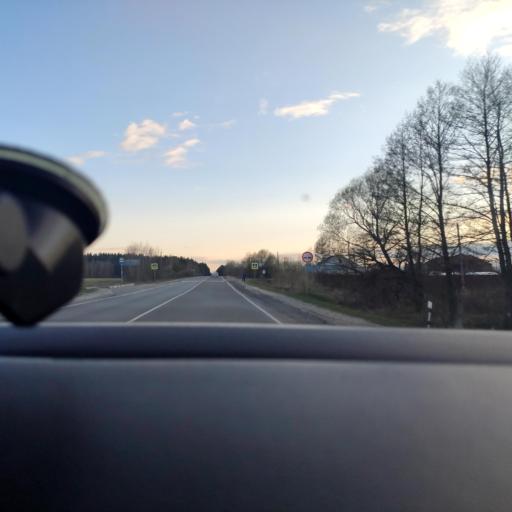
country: RU
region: Moskovskaya
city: Krasnyy Tkach
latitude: 55.4235
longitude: 39.1882
